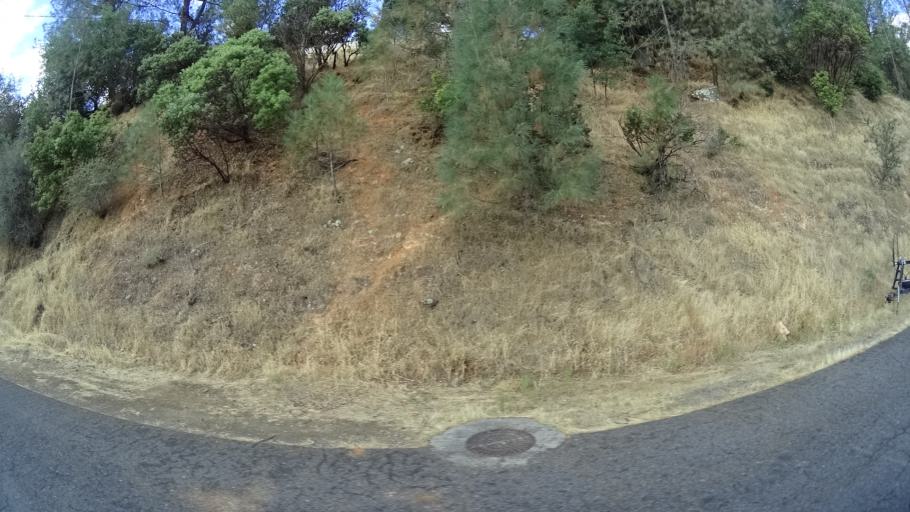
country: US
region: California
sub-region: Calaveras County
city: Copperopolis
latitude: 37.9087
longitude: -120.6016
